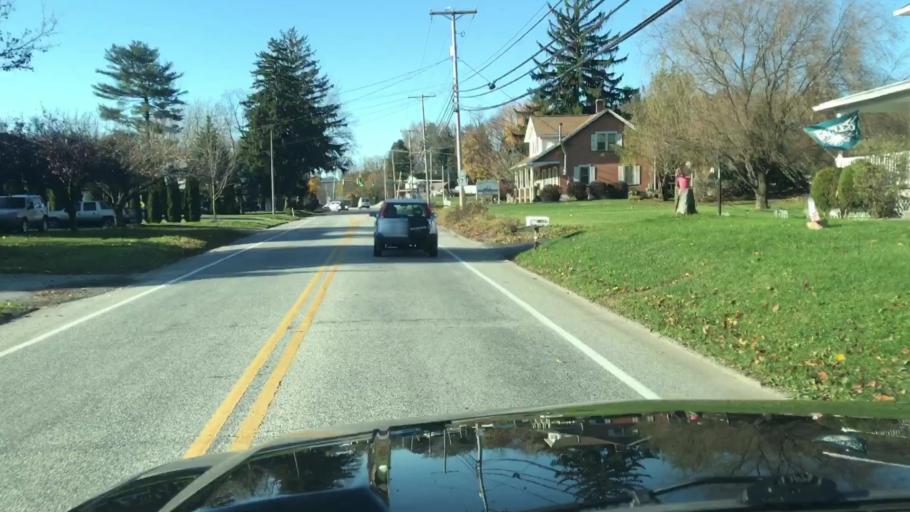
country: US
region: Pennsylvania
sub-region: York County
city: Valley Green
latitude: 40.1705
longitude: -76.8260
